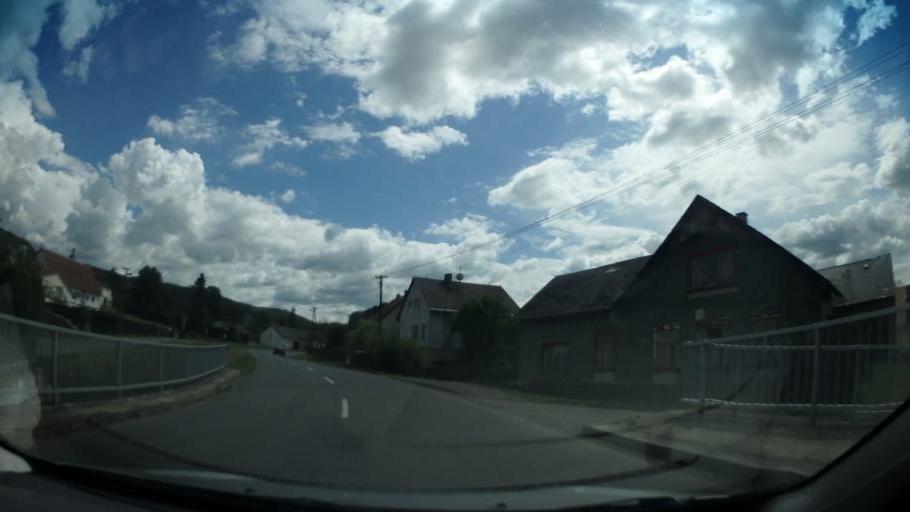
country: CZ
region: Pardubicky
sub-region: Okres Svitavy
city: Moravska Trebova
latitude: 49.7321
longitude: 16.6431
